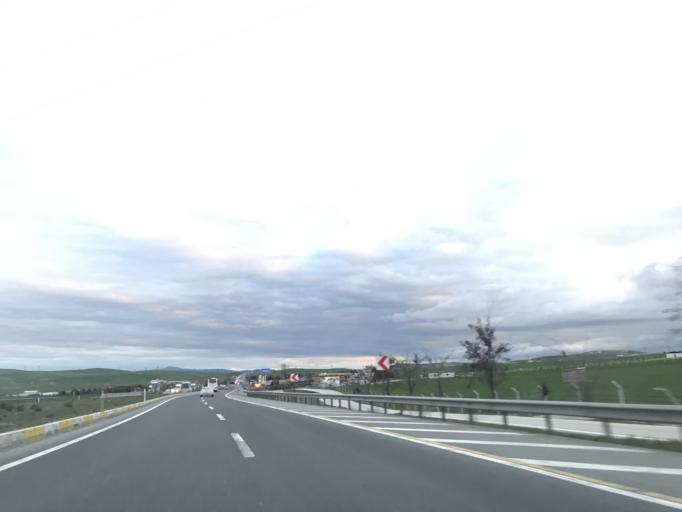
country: TR
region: Ankara
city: Ikizce
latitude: 39.4972
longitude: 32.8712
